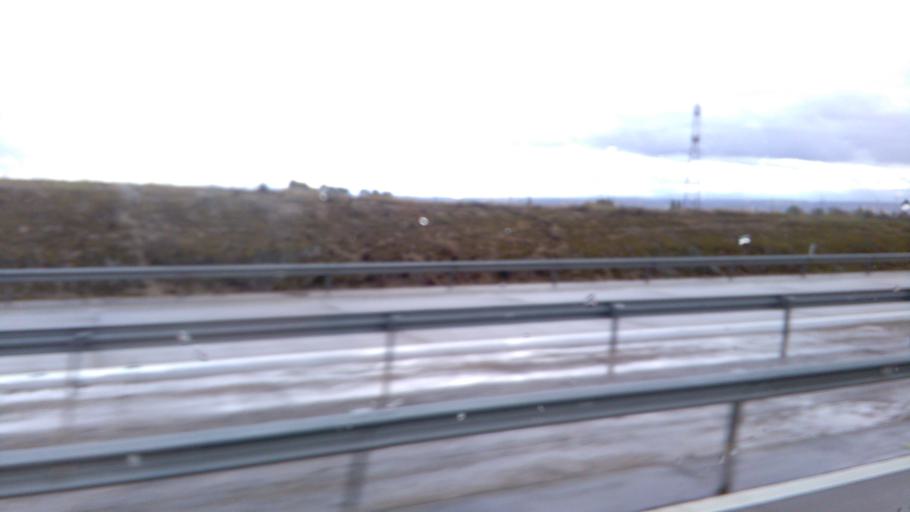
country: ES
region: Castille-La Mancha
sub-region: Province of Toledo
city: Cervera de los Montes
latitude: 40.0121
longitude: -4.8119
